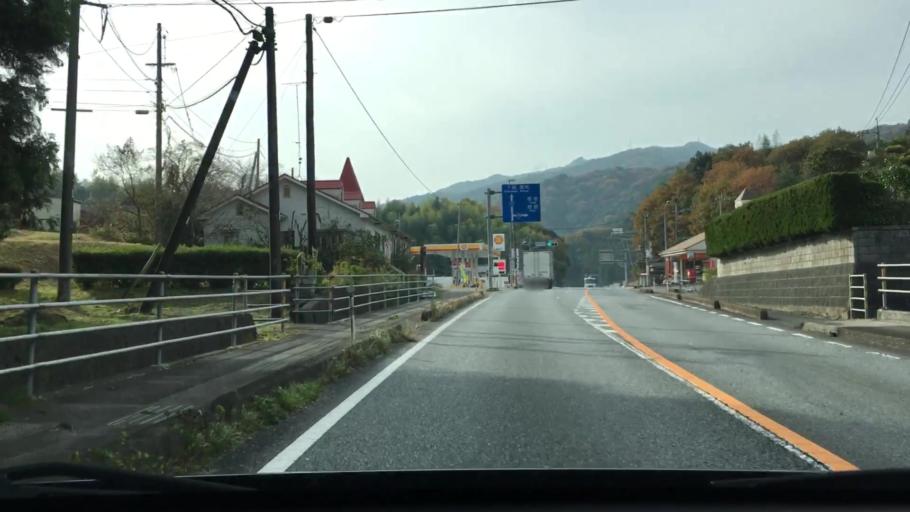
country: JP
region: Yamaguchi
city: Hikari
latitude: 34.0915
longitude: 132.0116
